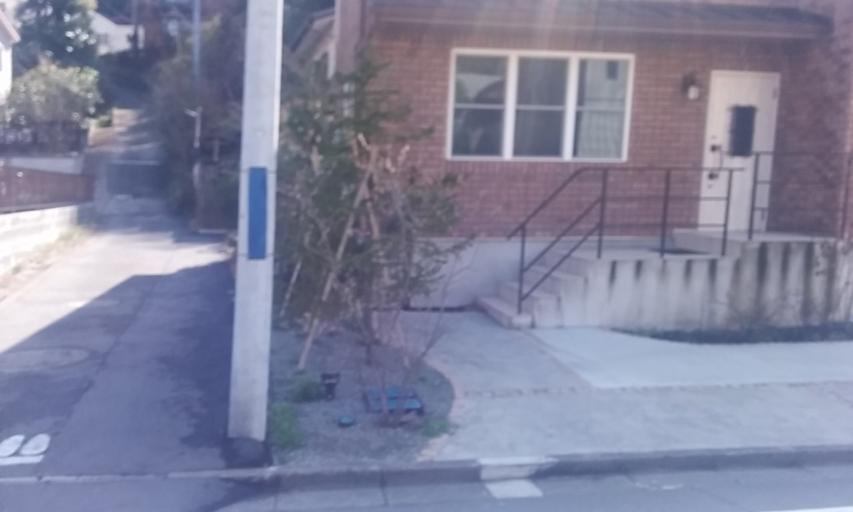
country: JP
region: Kanagawa
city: Kamakura
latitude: 35.3186
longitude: 139.5380
